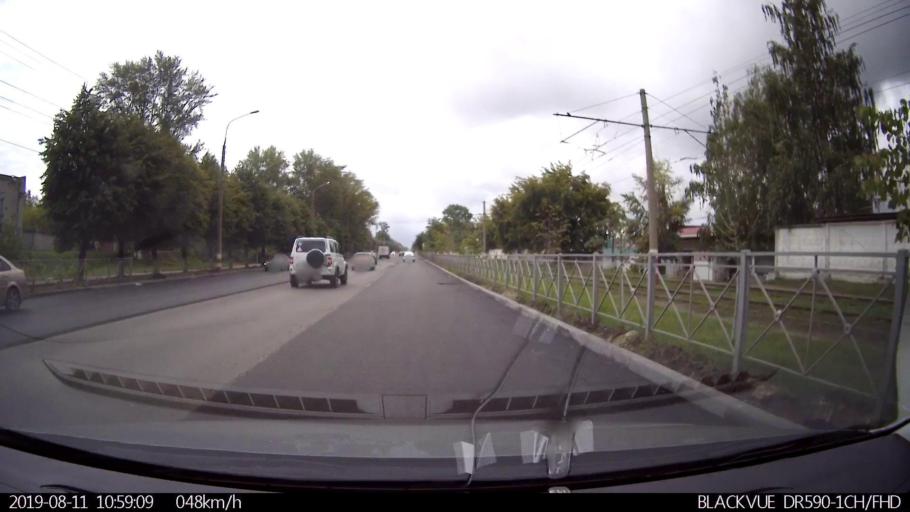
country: RU
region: Ulyanovsk
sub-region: Ulyanovskiy Rayon
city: Ulyanovsk
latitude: 54.2522
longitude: 48.3169
